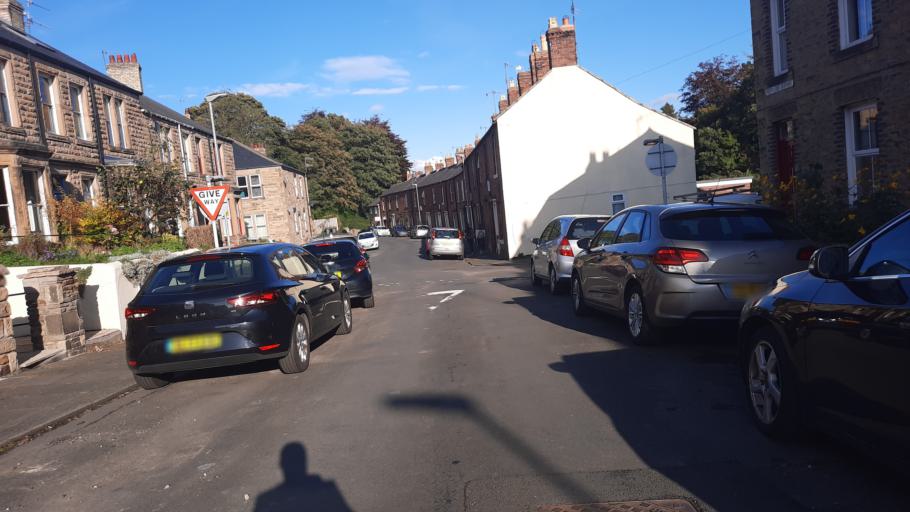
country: GB
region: England
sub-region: Northumberland
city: Hexham
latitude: 54.9719
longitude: -2.1114
